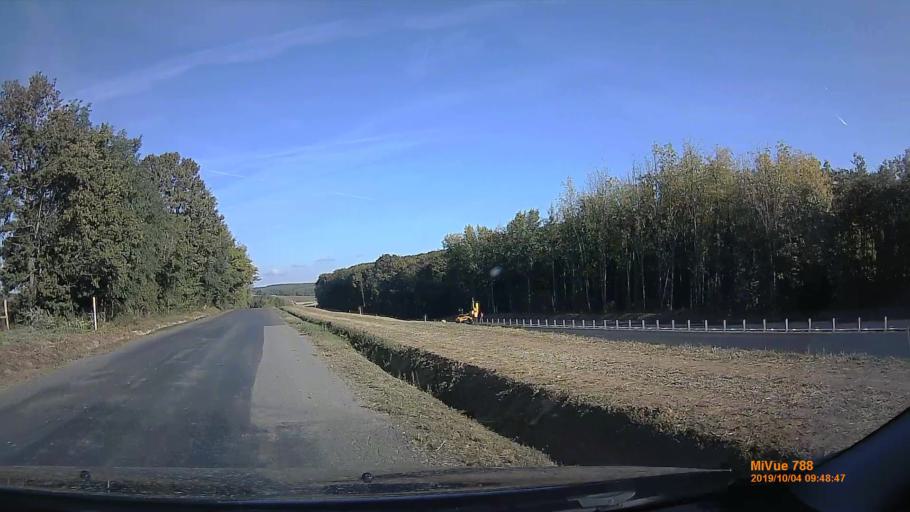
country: HU
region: Somogy
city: Kaposvar
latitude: 46.4400
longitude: 17.7702
